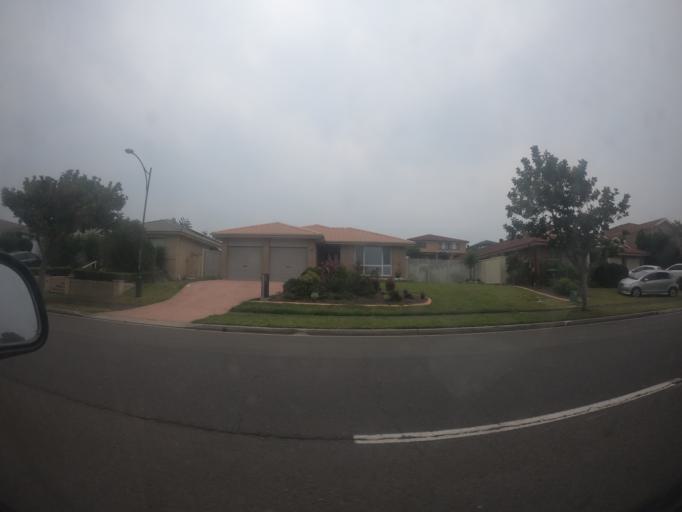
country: AU
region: New South Wales
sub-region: Shellharbour
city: Flinders
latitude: -34.5933
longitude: 150.8557
